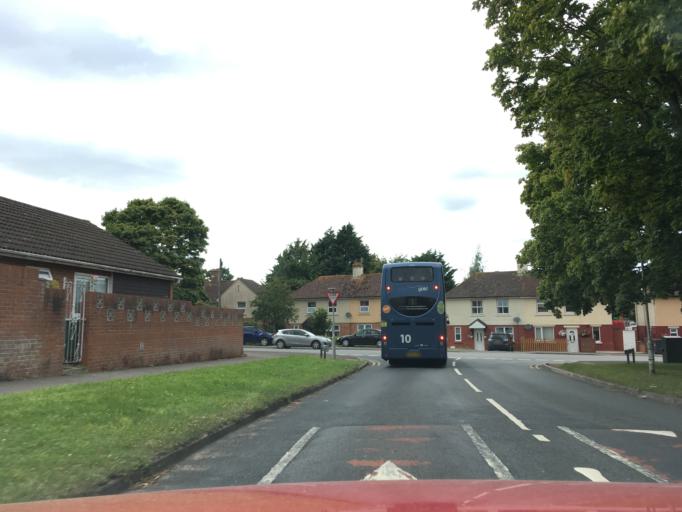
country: GB
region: England
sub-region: Gloucestershire
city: Gloucester
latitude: 51.8440
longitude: -2.2302
